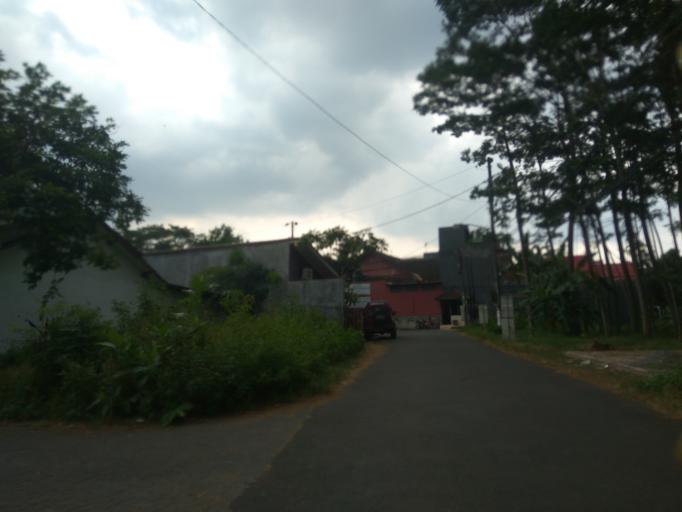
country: ID
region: Central Java
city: Semarang
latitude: -7.0644
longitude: 110.4472
